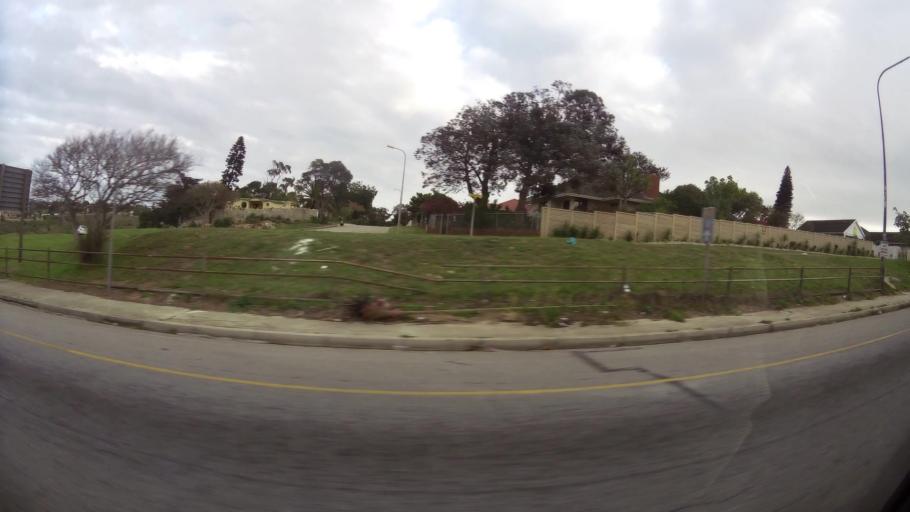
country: ZA
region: Eastern Cape
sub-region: Nelson Mandela Bay Metropolitan Municipality
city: Port Elizabeth
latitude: -33.9489
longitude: 25.5549
